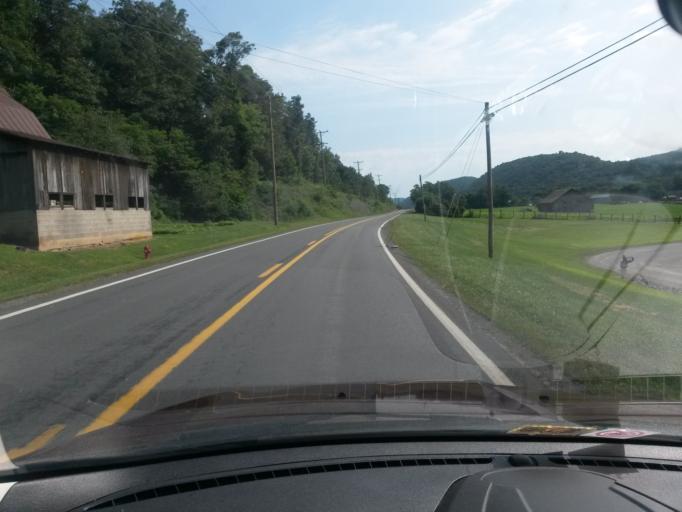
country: US
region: Virginia
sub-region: Shenandoah County
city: Basye
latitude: 38.9944
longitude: -78.7793
